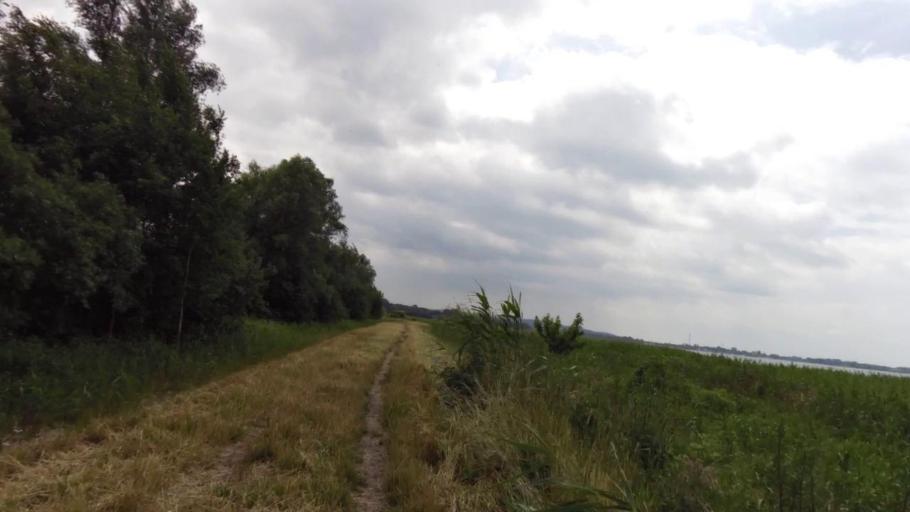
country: PL
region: West Pomeranian Voivodeship
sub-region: Szczecin
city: Szczecin
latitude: 53.4123
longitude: 14.6631
